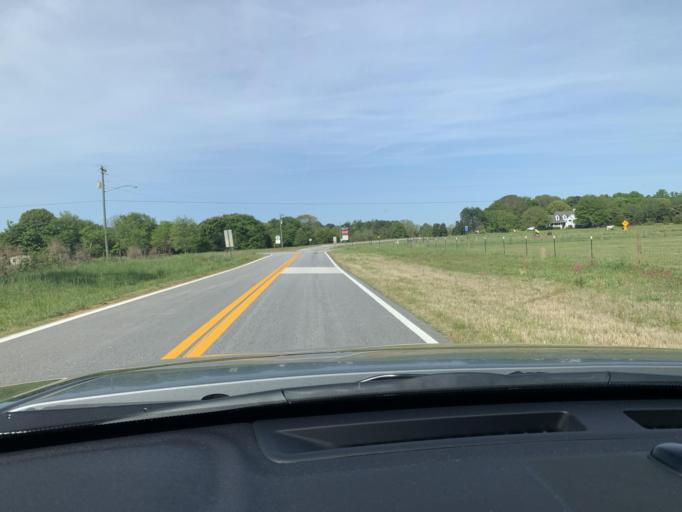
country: US
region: Georgia
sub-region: Oconee County
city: Watkinsville
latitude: 33.8120
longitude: -83.4005
